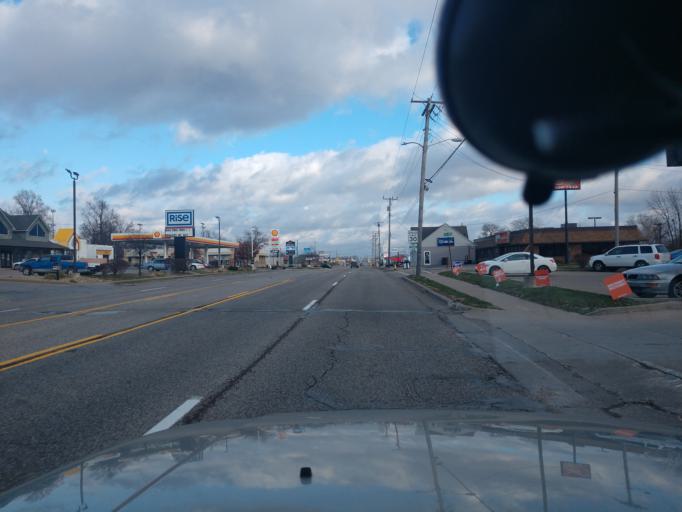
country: US
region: Illinois
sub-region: Adams County
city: Quincy
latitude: 39.9353
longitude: -91.3725
